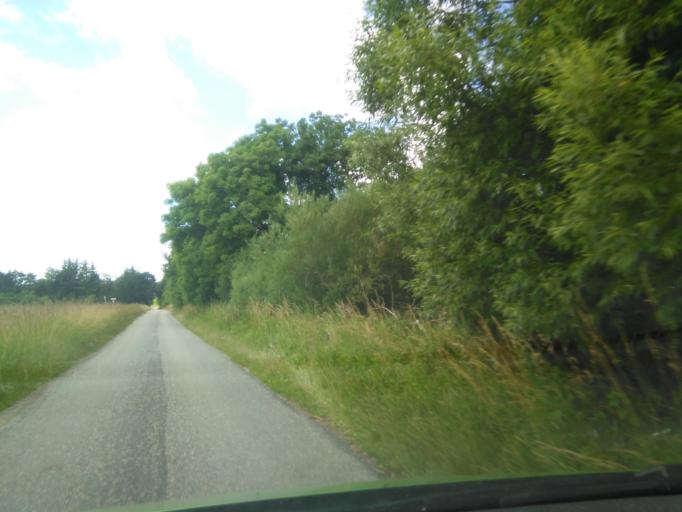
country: DK
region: Central Jutland
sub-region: Arhus Kommune
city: Logten
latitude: 56.1962
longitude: 10.3614
